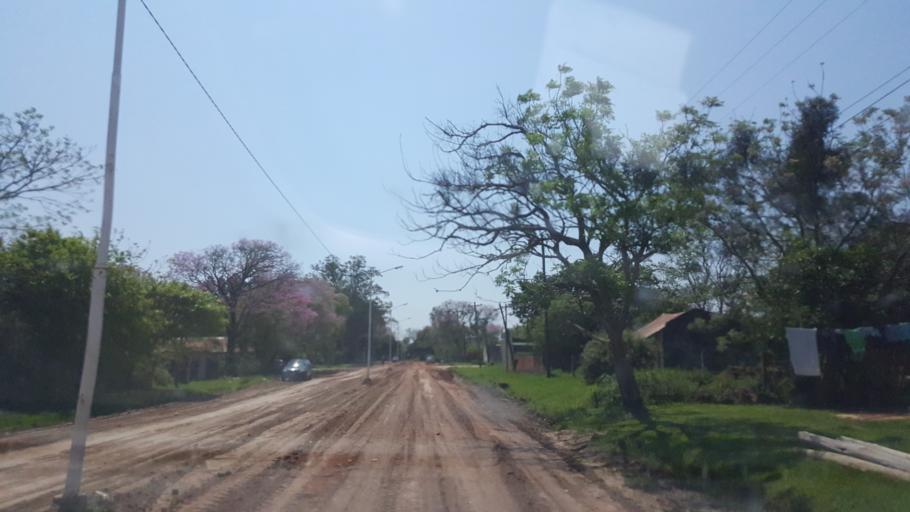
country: AR
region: Corrientes
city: Ita Ibate
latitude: -27.4268
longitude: -57.3421
